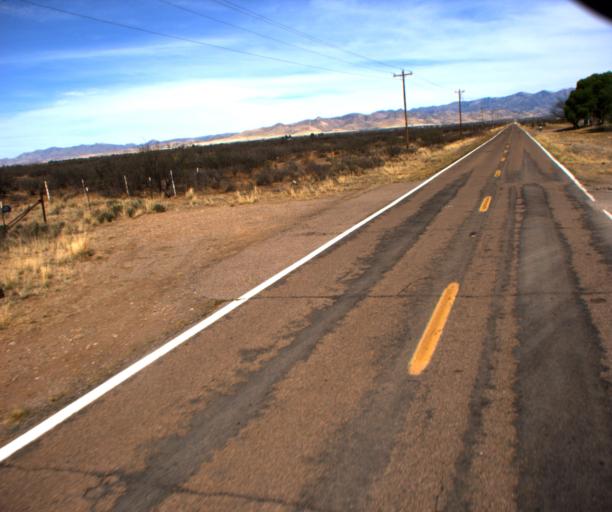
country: US
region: Arizona
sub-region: Cochise County
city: Willcox
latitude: 31.8760
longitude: -109.5766
